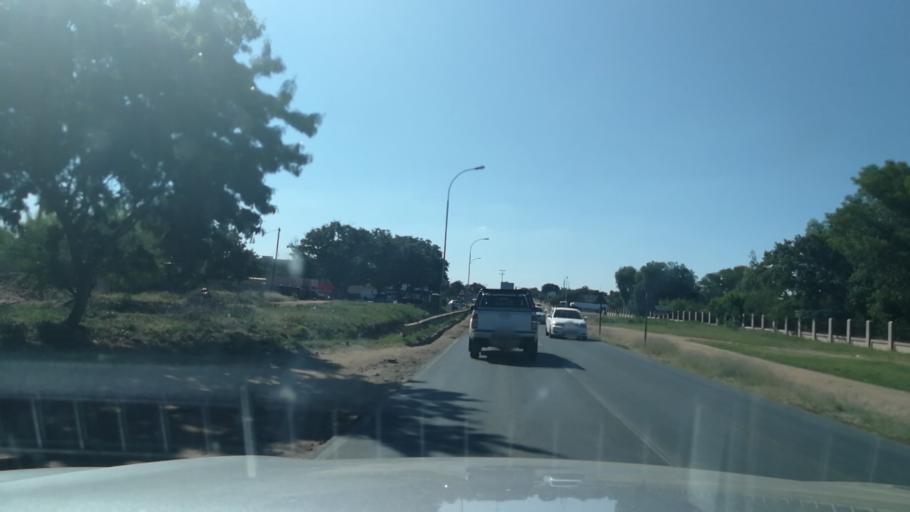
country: BW
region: South East
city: Gaborone
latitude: -24.6836
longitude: 25.9057
